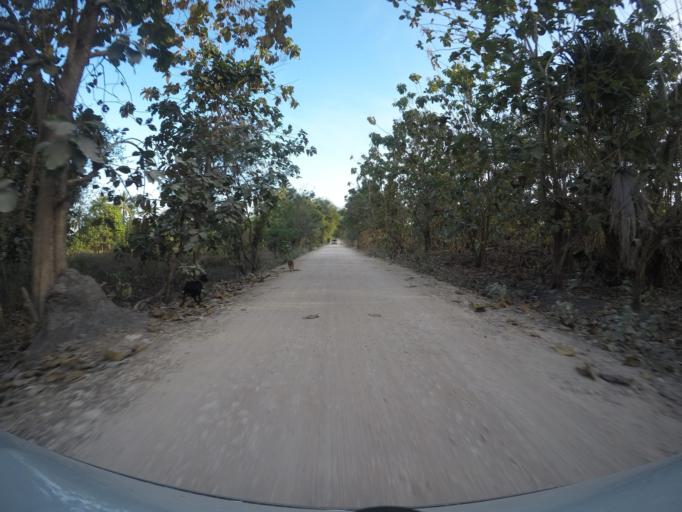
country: TL
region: Viqueque
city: Viqueque
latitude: -8.8816
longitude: 126.5074
